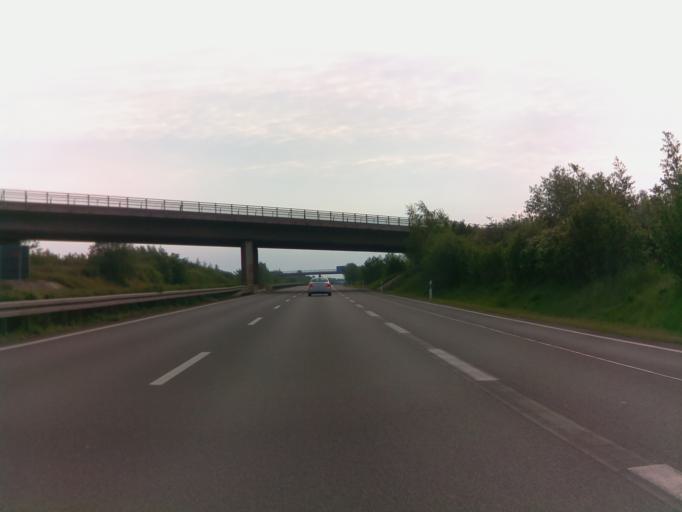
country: DE
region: Lower Saxony
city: Cremlingen
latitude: 52.2512
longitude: 10.6335
